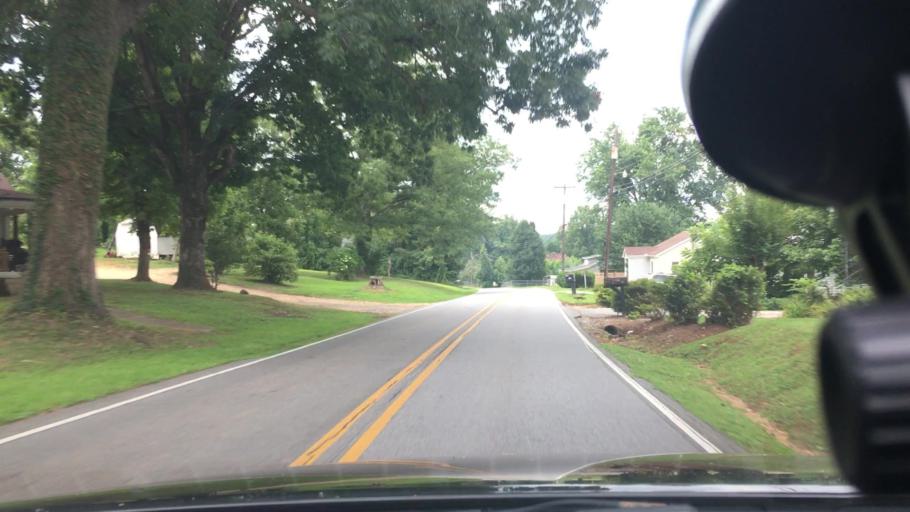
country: US
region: North Carolina
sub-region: McDowell County
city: West Marion
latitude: 35.6659
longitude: -82.0174
